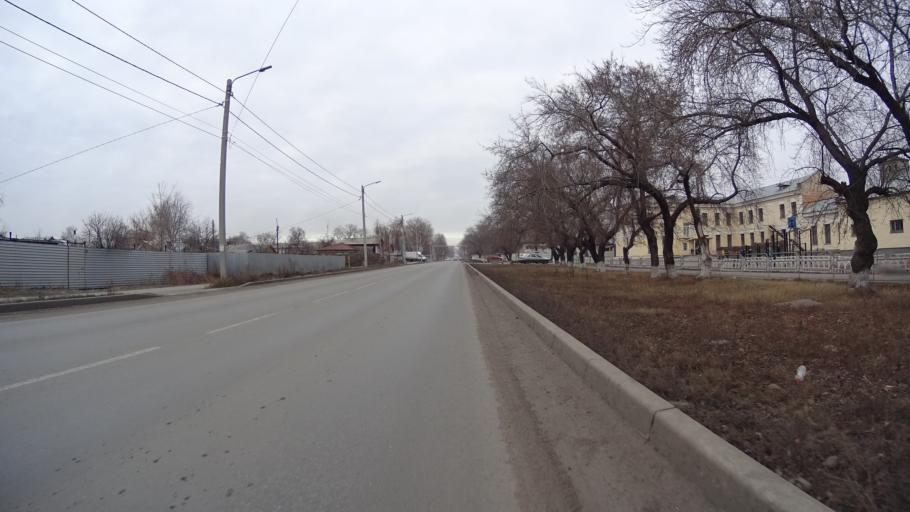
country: RU
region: Chelyabinsk
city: Troitsk
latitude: 54.1097
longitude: 61.5704
